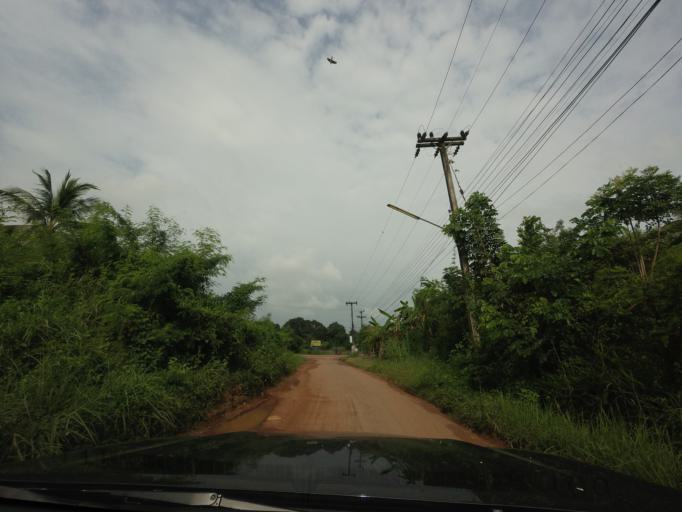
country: TH
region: Nong Khai
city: Nong Khai
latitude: 17.8155
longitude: 102.7195
